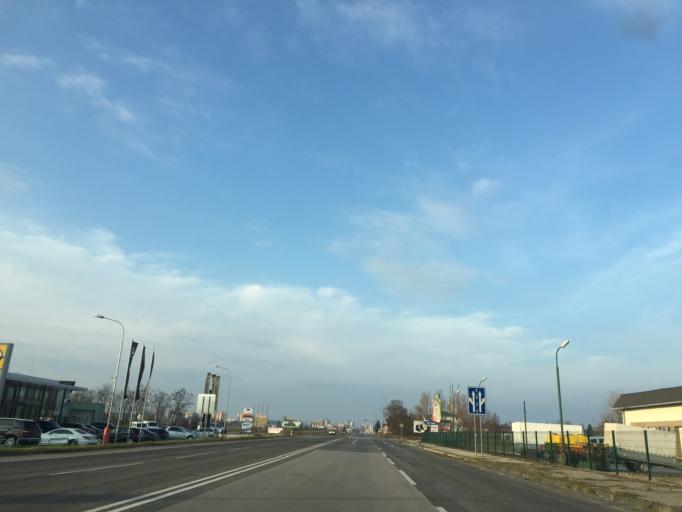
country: SK
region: Nitriansky
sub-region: Okres Nove Zamky
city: Nove Zamky
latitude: 47.9667
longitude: 18.1848
